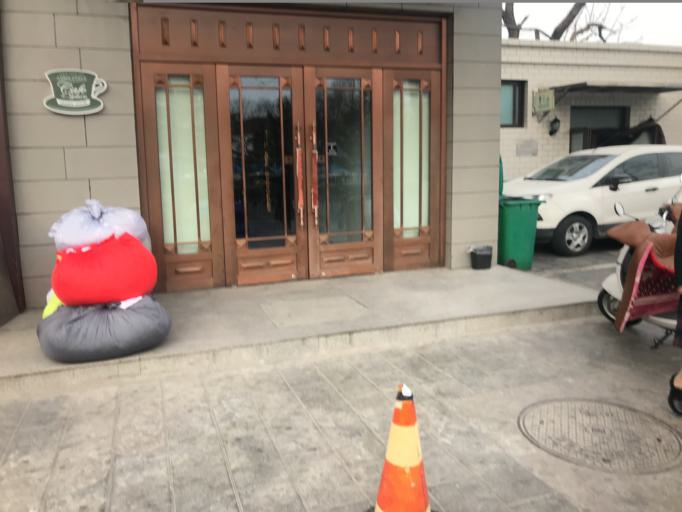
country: CN
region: Beijing
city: Beijing
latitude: 39.8888
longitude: 116.3864
